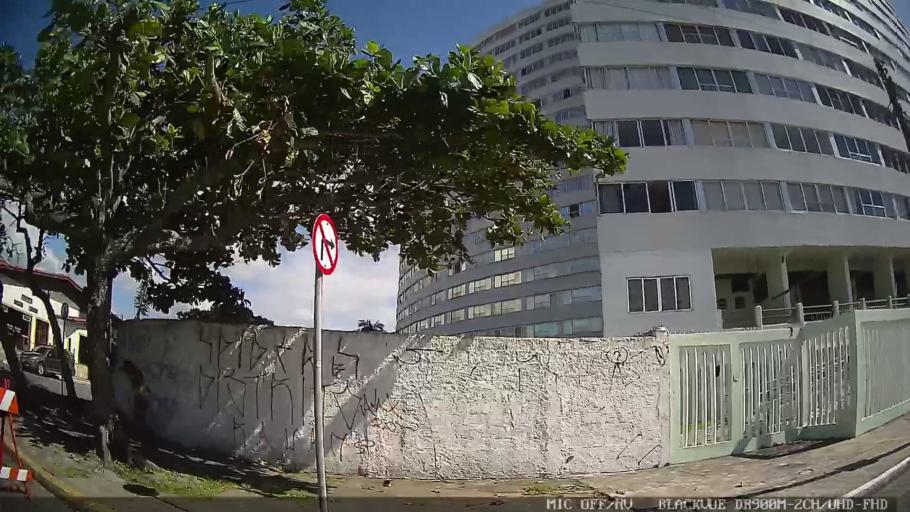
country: BR
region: Sao Paulo
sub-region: Peruibe
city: Peruibe
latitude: -24.3256
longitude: -46.9962
